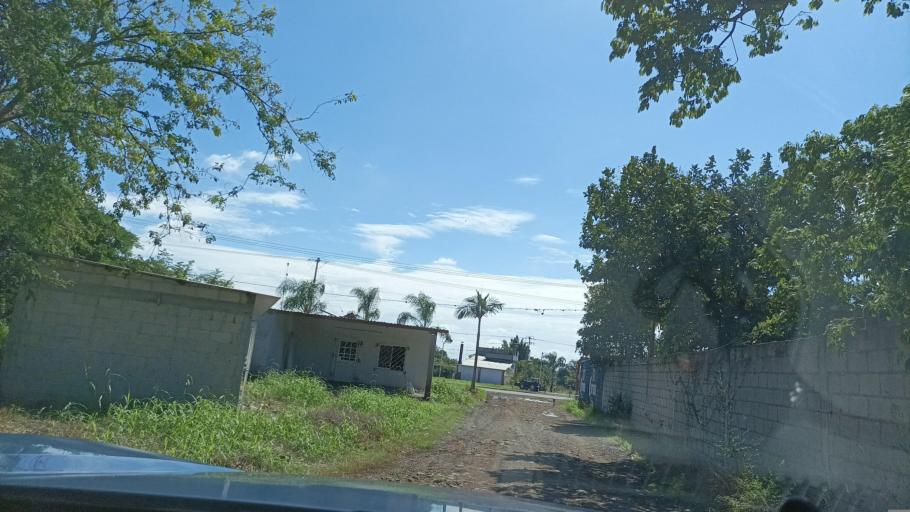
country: MX
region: Veracruz
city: Paso del Macho
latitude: 18.9655
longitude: -96.7344
